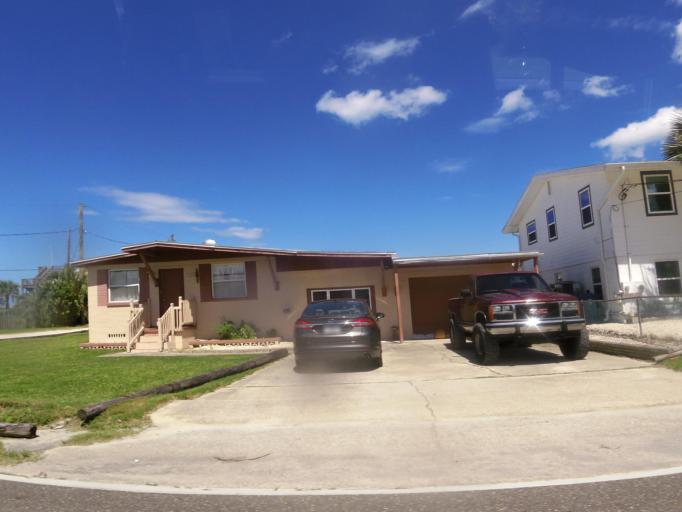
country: US
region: Florida
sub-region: Nassau County
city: Fernandina Beach
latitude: 30.6742
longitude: -81.4307
